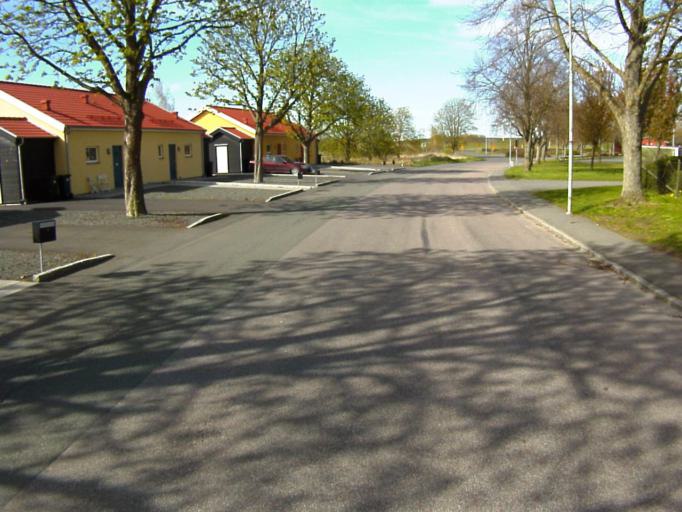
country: SE
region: Skane
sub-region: Kristianstads Kommun
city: Kristianstad
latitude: 56.0596
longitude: 14.1516
